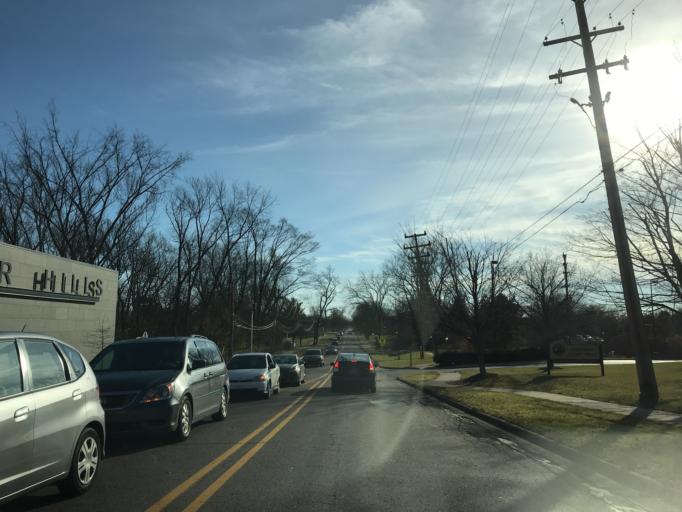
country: US
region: Michigan
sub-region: Washtenaw County
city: Ann Arbor
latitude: 42.2574
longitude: -83.7003
